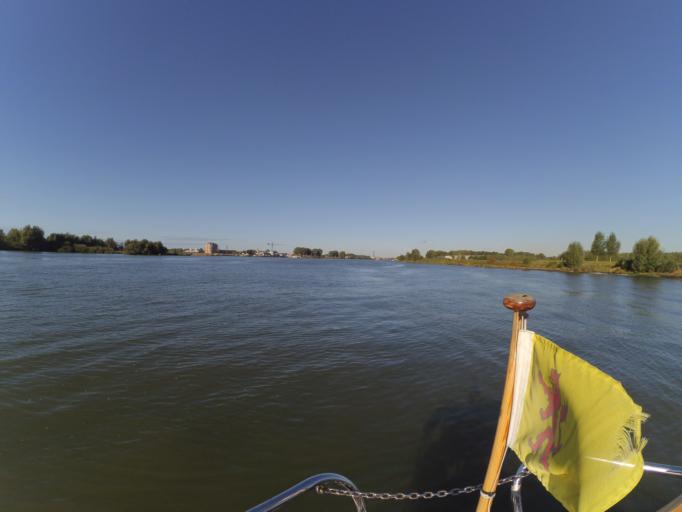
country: NL
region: South Holland
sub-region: Gemeente Zwijndrecht
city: Heerjansdam
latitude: 51.8076
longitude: 4.5885
